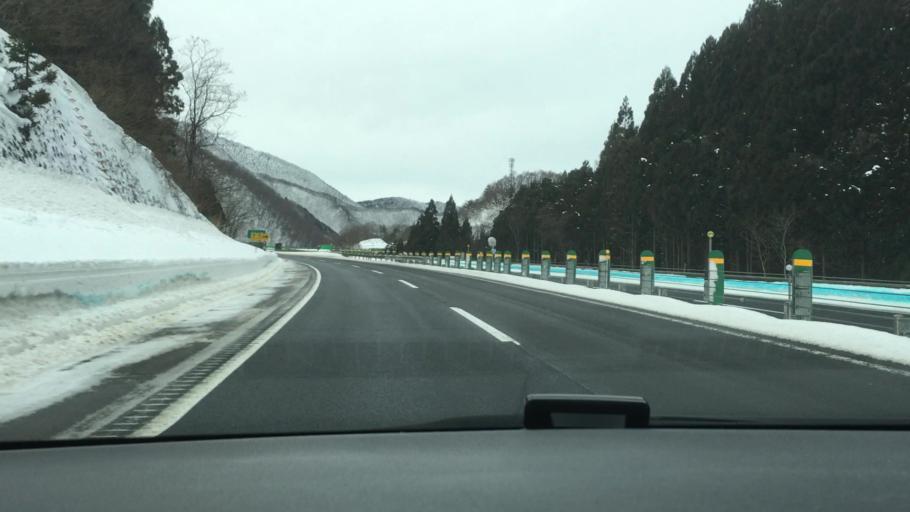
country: JP
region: Akita
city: Hanawa
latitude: 40.1204
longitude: 140.8506
